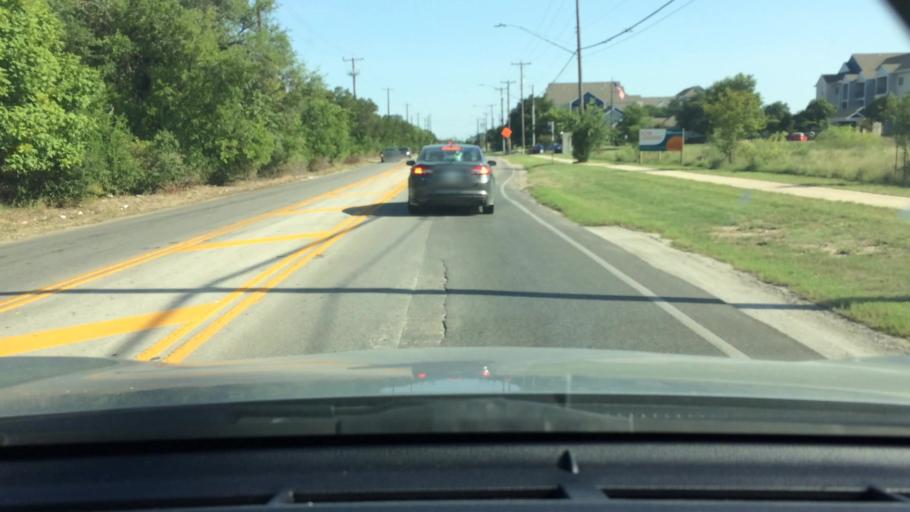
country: US
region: Texas
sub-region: Bexar County
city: Helotes
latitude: 29.5759
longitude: -98.6318
